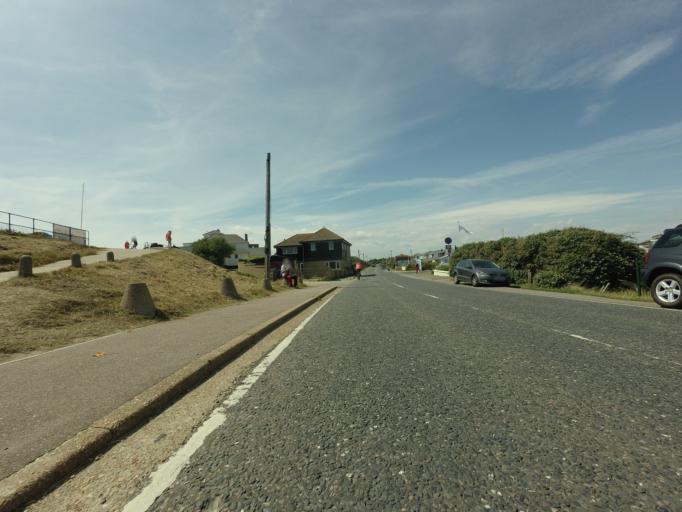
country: GB
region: England
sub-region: East Sussex
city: Rye
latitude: 50.9315
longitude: 0.8057
